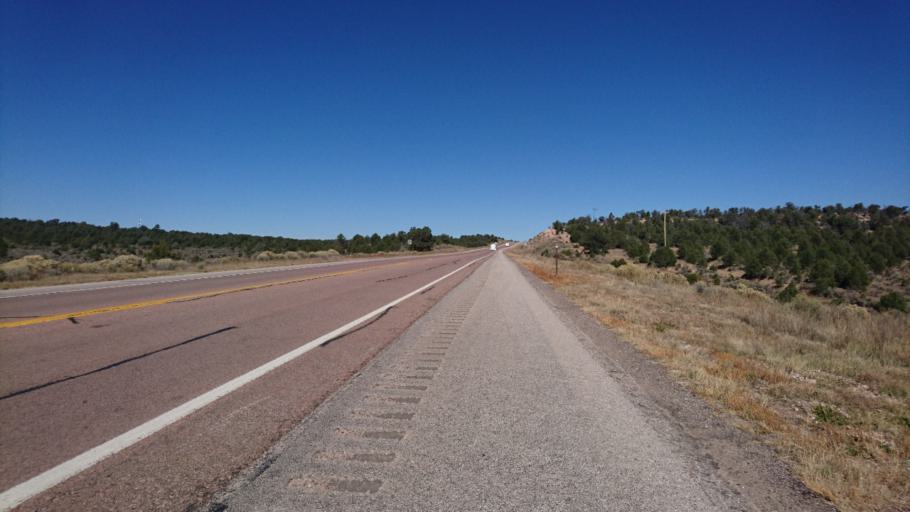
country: US
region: New Mexico
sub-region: McKinley County
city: Black Rock
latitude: 35.3014
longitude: -108.7573
